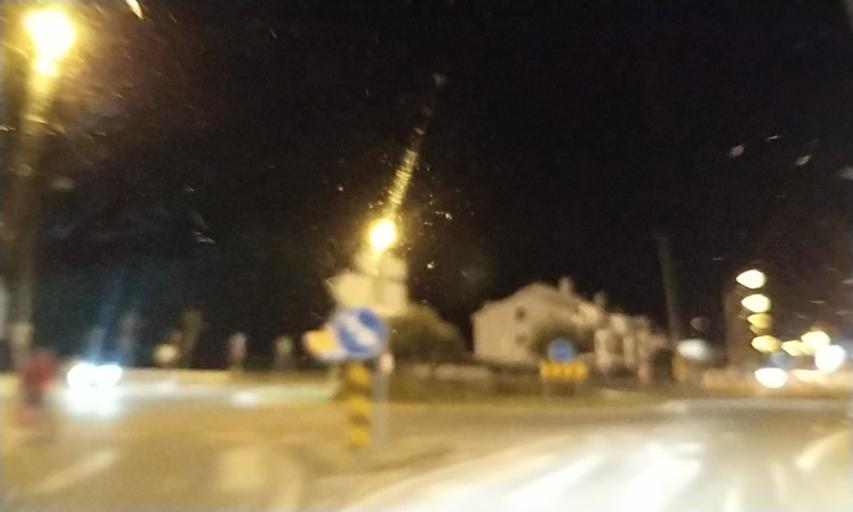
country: PT
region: Castelo Branco
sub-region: Concelho do Fundao
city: Fundao
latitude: 40.1552
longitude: -7.4972
